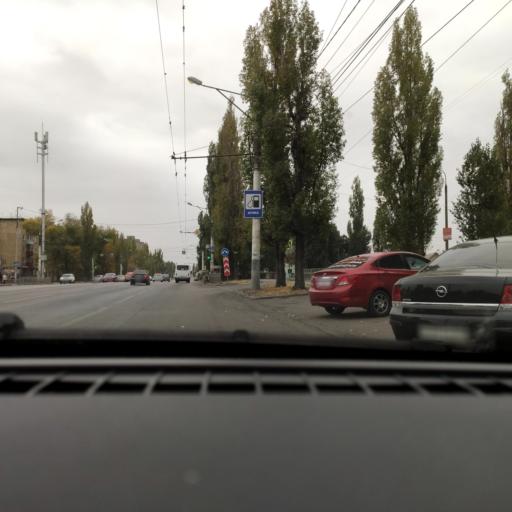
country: RU
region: Voronezj
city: Maslovka
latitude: 51.6109
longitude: 39.2371
